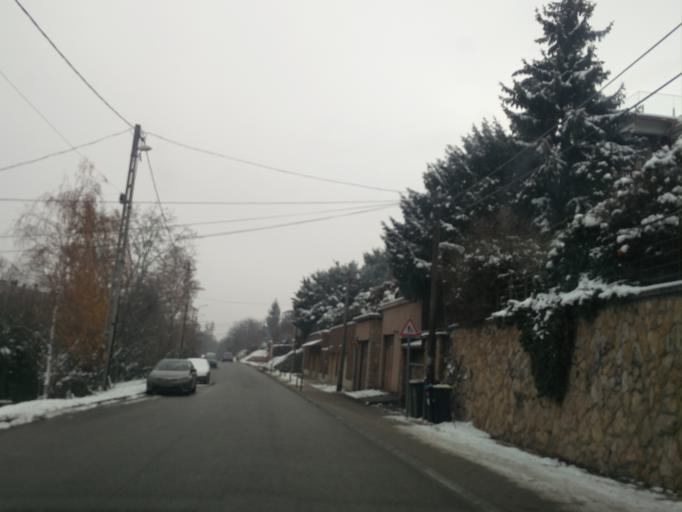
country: HU
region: Budapest
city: Budapest III. keruelet
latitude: 47.5386
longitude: 19.0224
